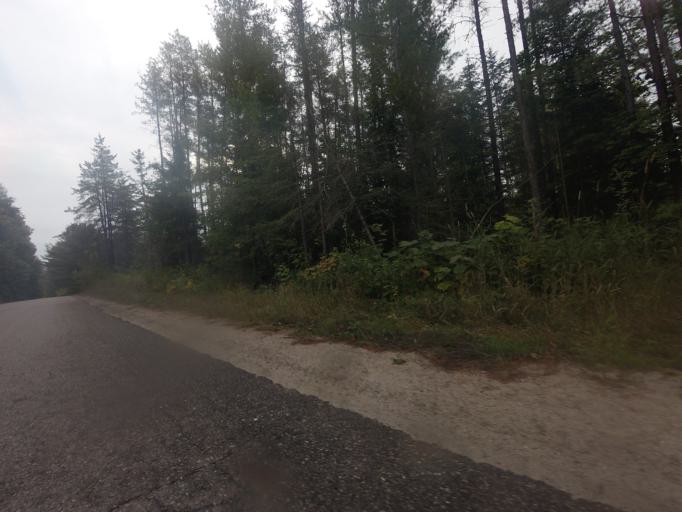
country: CA
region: Quebec
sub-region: Outaouais
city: Maniwaki
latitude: 46.0846
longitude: -76.0137
